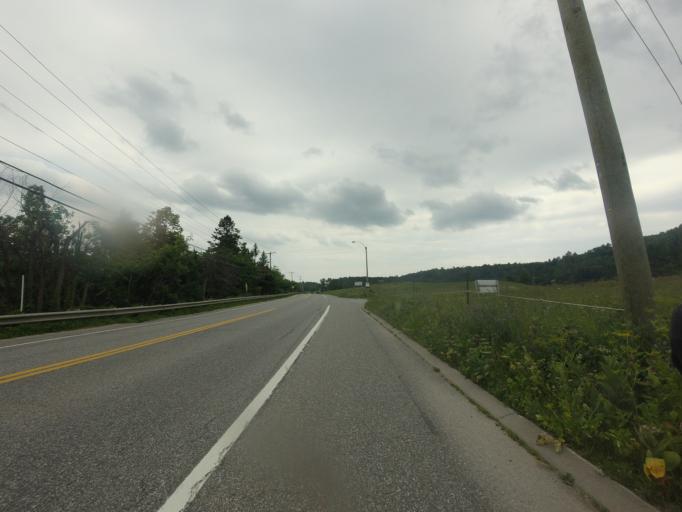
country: CA
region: Quebec
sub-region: Outaouais
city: Wakefield
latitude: 45.7386
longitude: -75.9082
